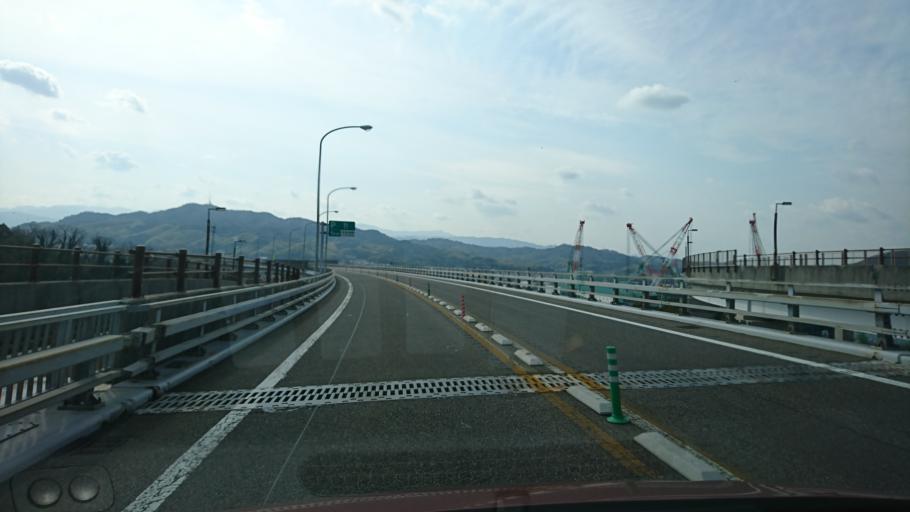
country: JP
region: Hiroshima
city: Takehara
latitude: 34.1113
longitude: 132.9771
